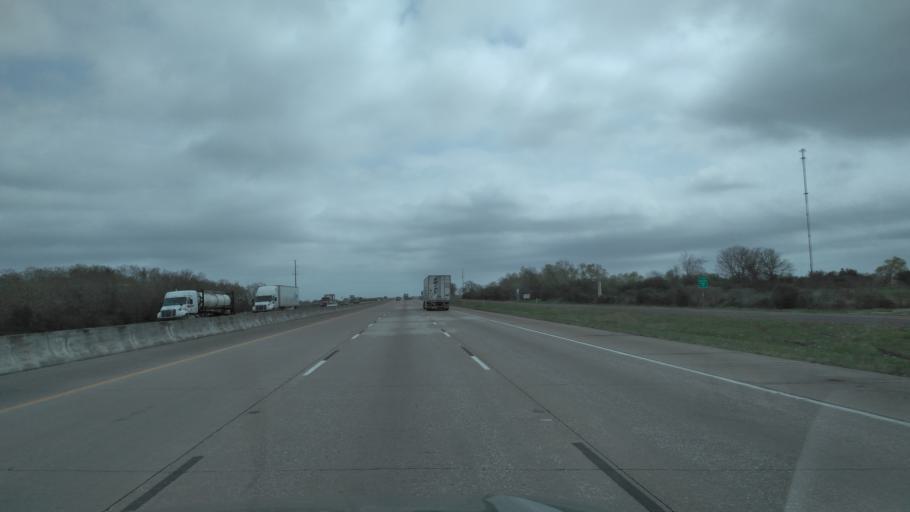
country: US
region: Texas
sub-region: Chambers County
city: Winnie
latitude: 29.8314
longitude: -94.5009
